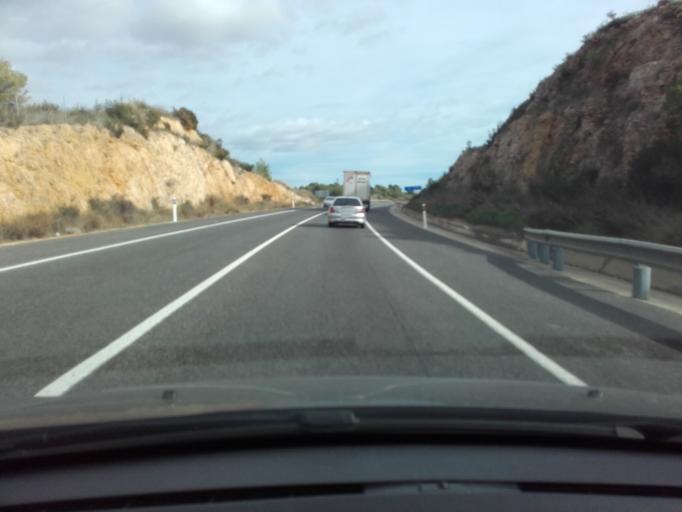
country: ES
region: Catalonia
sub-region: Provincia de Tarragona
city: Altafulla
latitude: 41.1560
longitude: 1.3726
